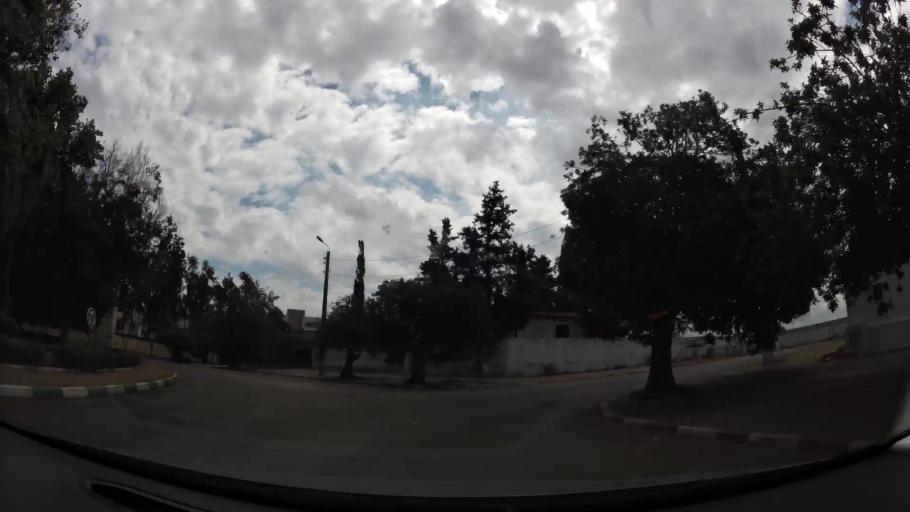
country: MA
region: Gharb-Chrarda-Beni Hssen
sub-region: Kenitra Province
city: Kenitra
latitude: 34.2522
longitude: -6.5850
